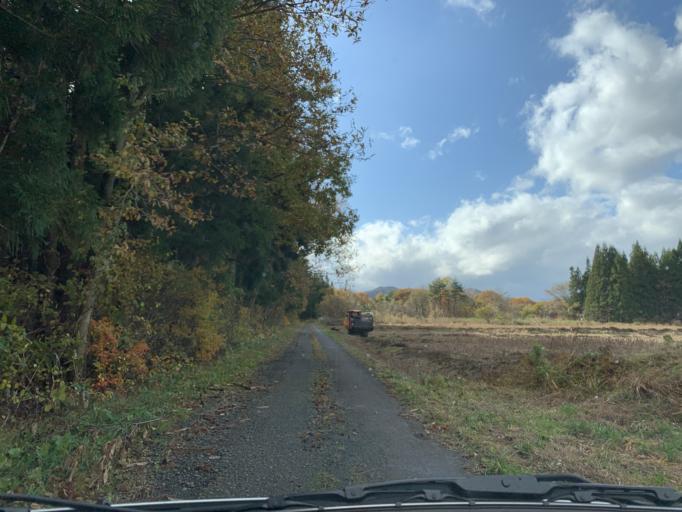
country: JP
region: Iwate
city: Mizusawa
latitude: 39.1170
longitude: 140.9672
